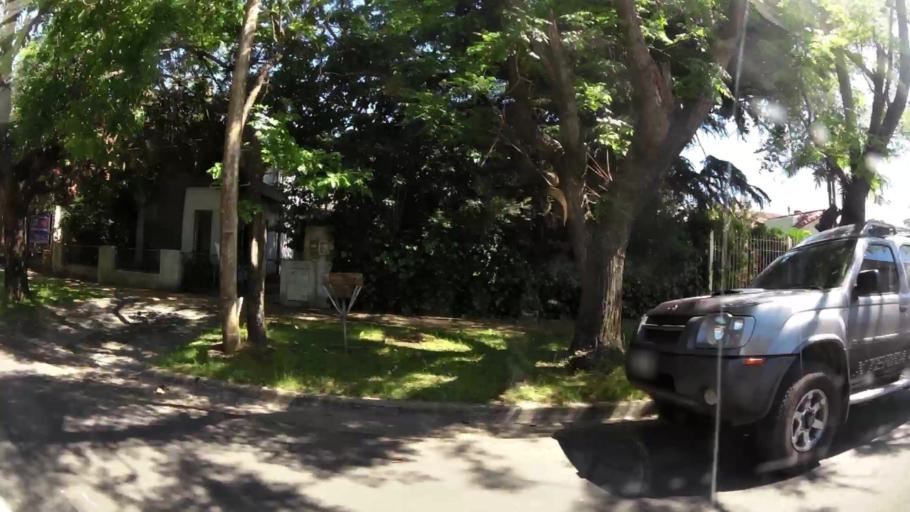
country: AR
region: Buenos Aires
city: Ituzaingo
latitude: -34.6652
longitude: -58.6675
